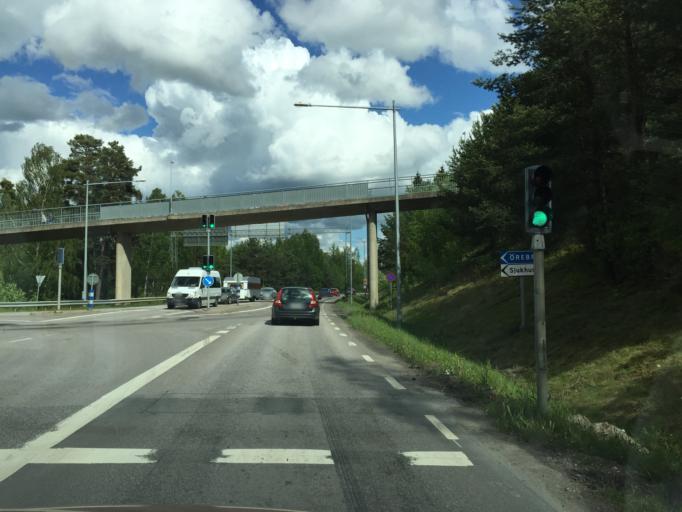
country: SE
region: OEstergoetland
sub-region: Finspangs Kommun
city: Finspang
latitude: 58.7041
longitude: 15.7679
